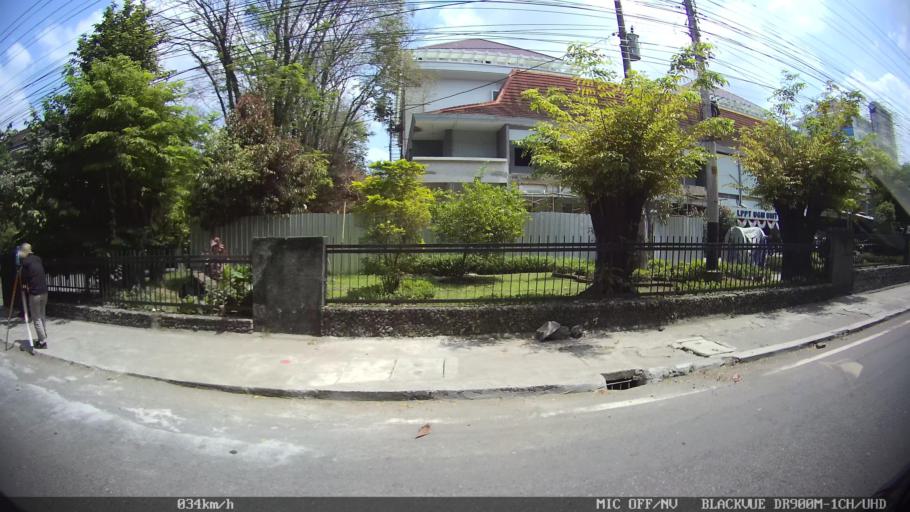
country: ID
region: Daerah Istimewa Yogyakarta
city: Yogyakarta
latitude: -7.7706
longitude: 110.3766
